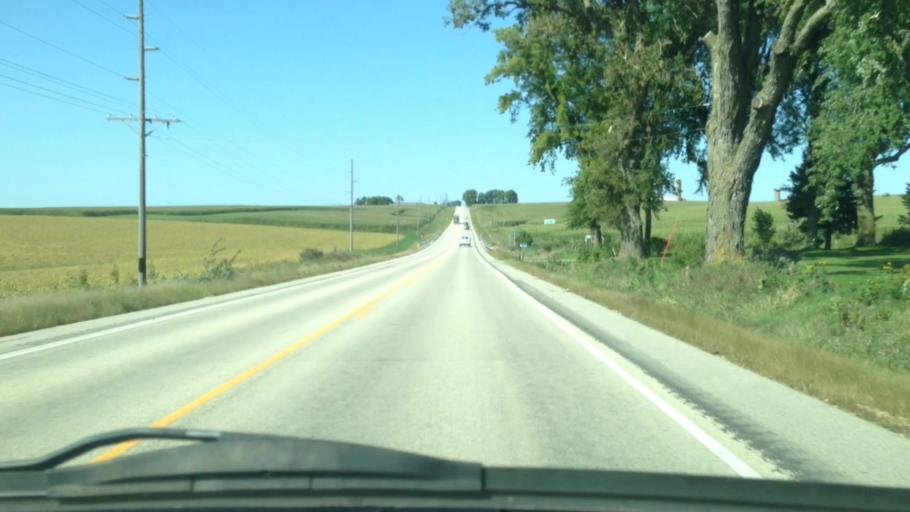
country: US
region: Minnesota
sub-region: Fillmore County
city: Rushford
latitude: 43.9084
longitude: -91.7401
